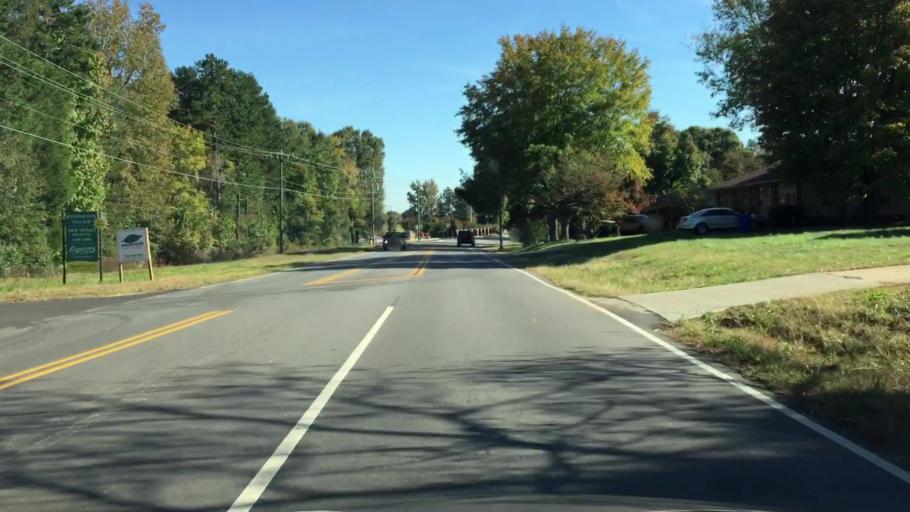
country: US
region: North Carolina
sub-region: Iredell County
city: Mooresville
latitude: 35.5788
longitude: -80.7941
